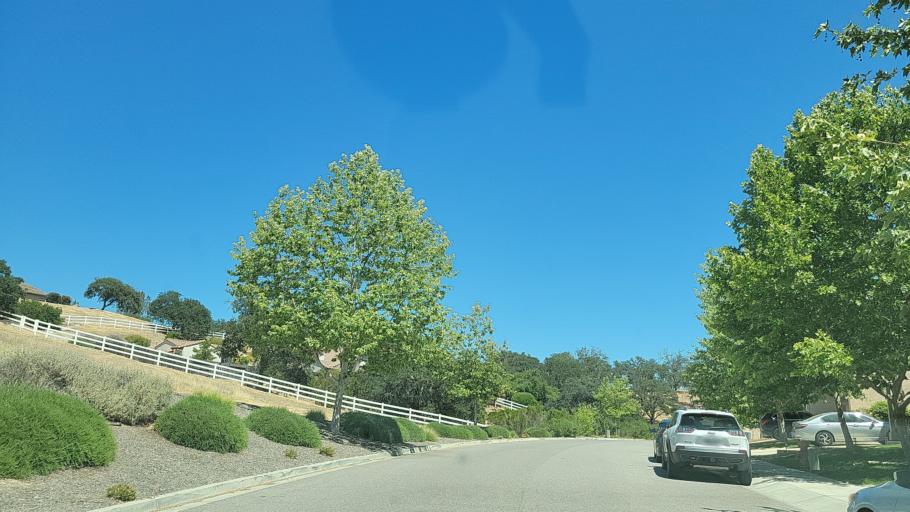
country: US
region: California
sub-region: San Luis Obispo County
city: Atascadero
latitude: 35.4559
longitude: -120.6275
